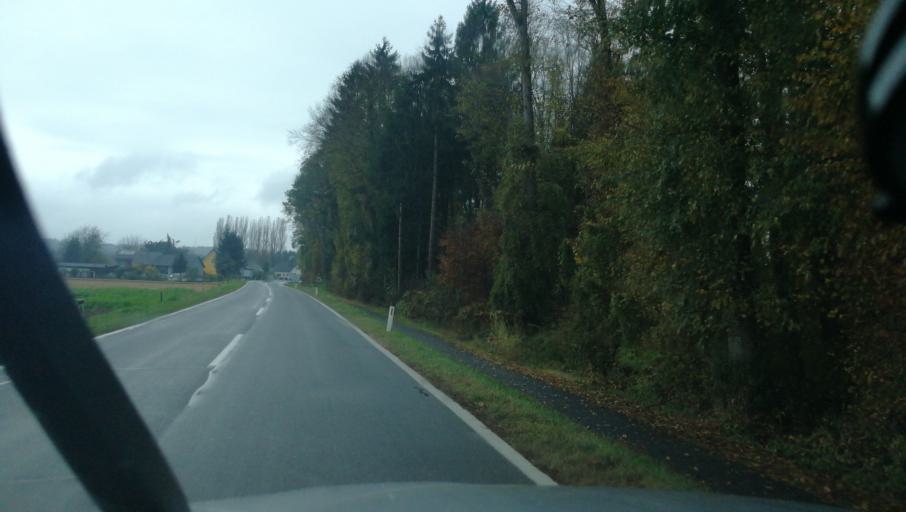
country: AT
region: Styria
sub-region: Politischer Bezirk Leibnitz
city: Strass in Steiermark
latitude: 46.7258
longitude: 15.6384
